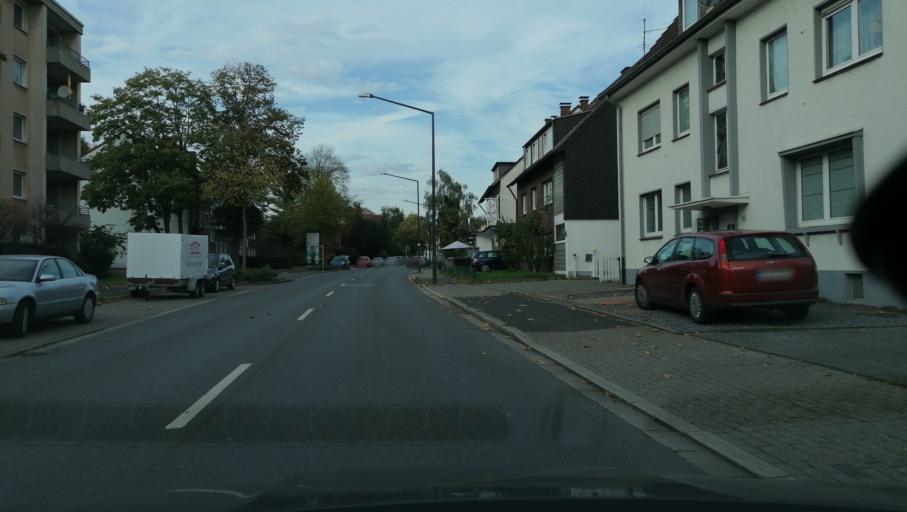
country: DE
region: North Rhine-Westphalia
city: Herten
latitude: 51.5880
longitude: 7.1480
